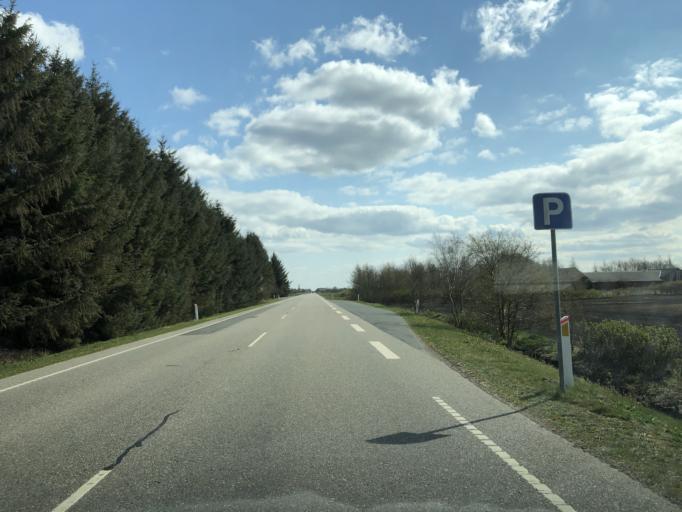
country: DK
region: Central Jutland
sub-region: Lemvig Kommune
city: Lemvig
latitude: 56.4244
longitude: 8.2452
